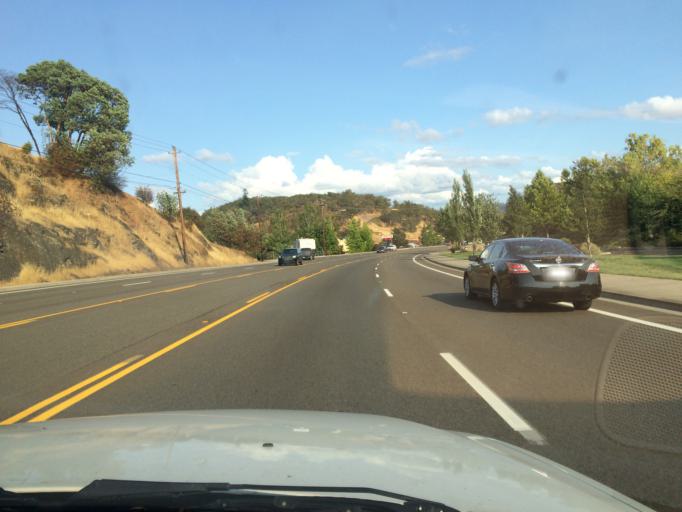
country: US
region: Oregon
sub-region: Douglas County
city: Roseburg
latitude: 43.2347
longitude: -123.3779
